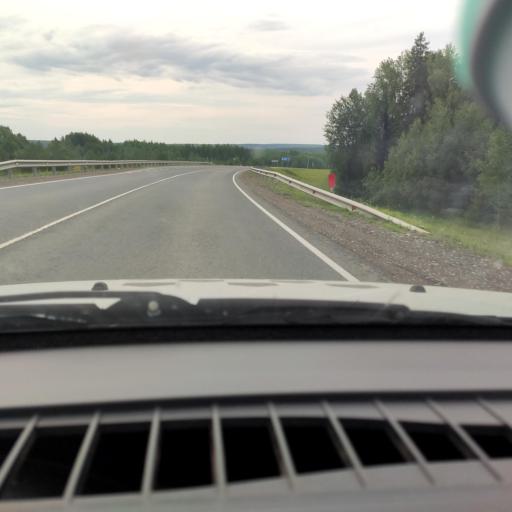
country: RU
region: Kirov
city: Kostino
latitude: 58.8121
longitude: 53.5934
